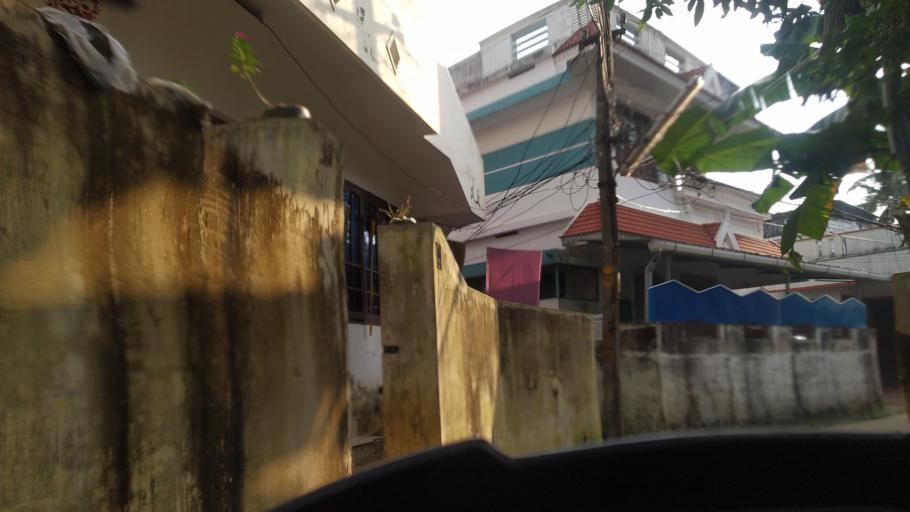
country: IN
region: Kerala
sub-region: Ernakulam
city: Cochin
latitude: 9.9836
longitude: 76.3110
